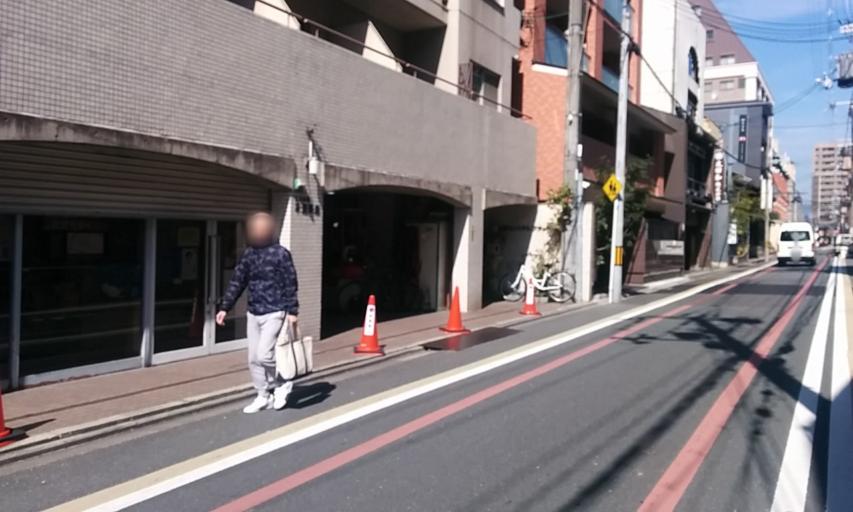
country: JP
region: Kyoto
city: Kyoto
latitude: 35.0074
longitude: 135.7625
